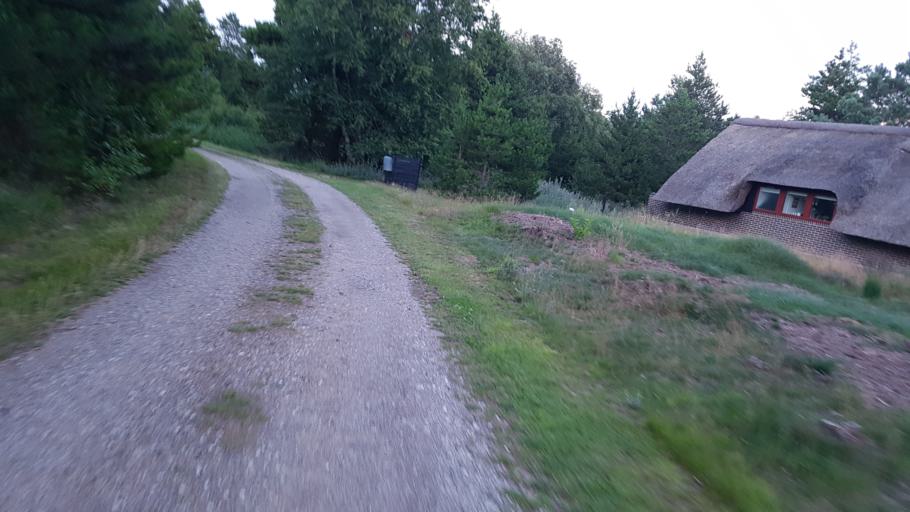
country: DE
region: Schleswig-Holstein
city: List
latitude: 55.0918
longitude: 8.5237
